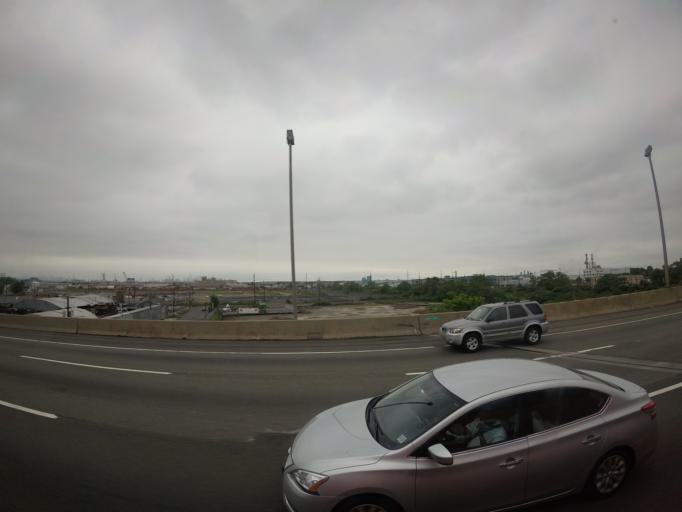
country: US
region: New Jersey
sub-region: Hudson County
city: Harrison
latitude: 40.7267
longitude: -74.1307
